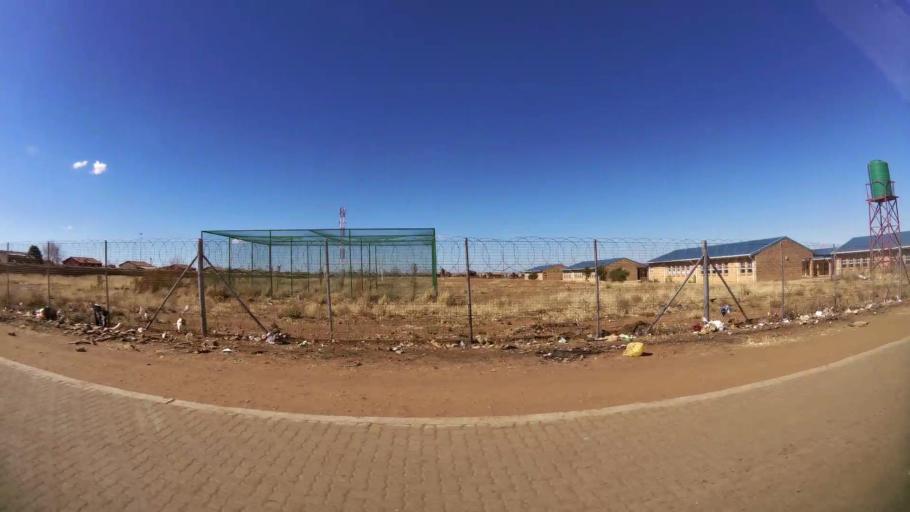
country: ZA
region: North-West
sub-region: Dr Kenneth Kaunda District Municipality
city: Klerksdorp
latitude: -26.8721
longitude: 26.5647
